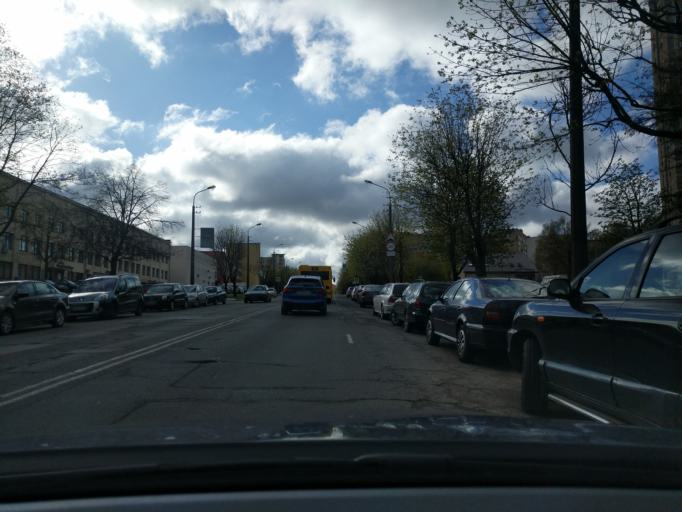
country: BY
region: Minsk
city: Novoye Medvezhino
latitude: 53.9163
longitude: 27.5033
